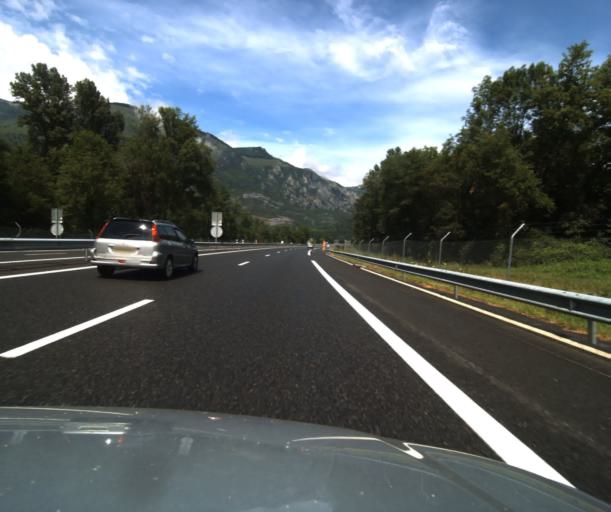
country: FR
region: Midi-Pyrenees
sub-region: Departement des Hautes-Pyrenees
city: Argeles-Gazost
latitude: 43.0186
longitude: -0.0869
